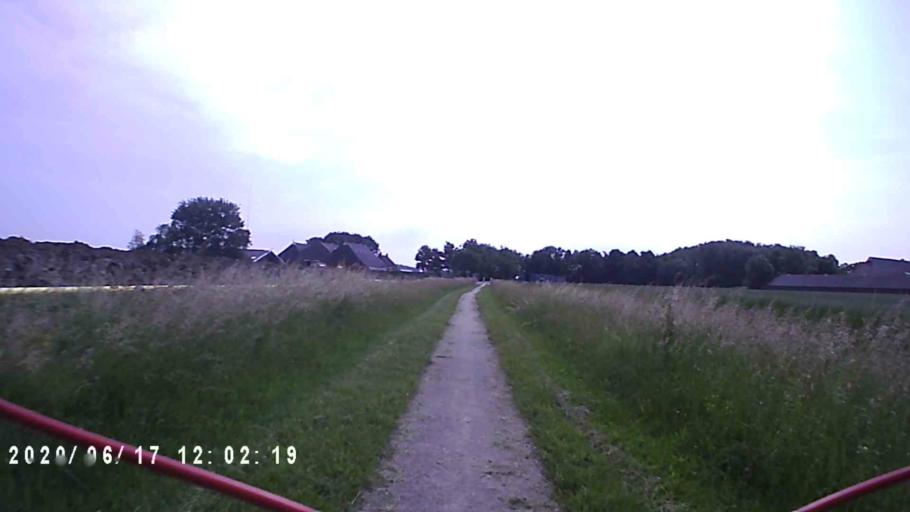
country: NL
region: Groningen
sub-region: Gemeente De Marne
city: Ulrum
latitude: 53.3402
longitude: 6.3397
